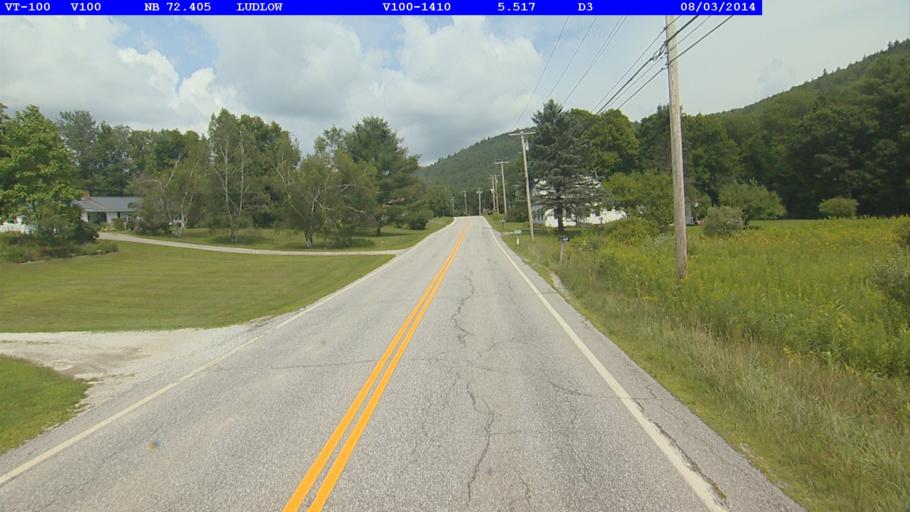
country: US
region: Vermont
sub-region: Windsor County
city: Chester
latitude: 43.4253
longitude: -72.7013
